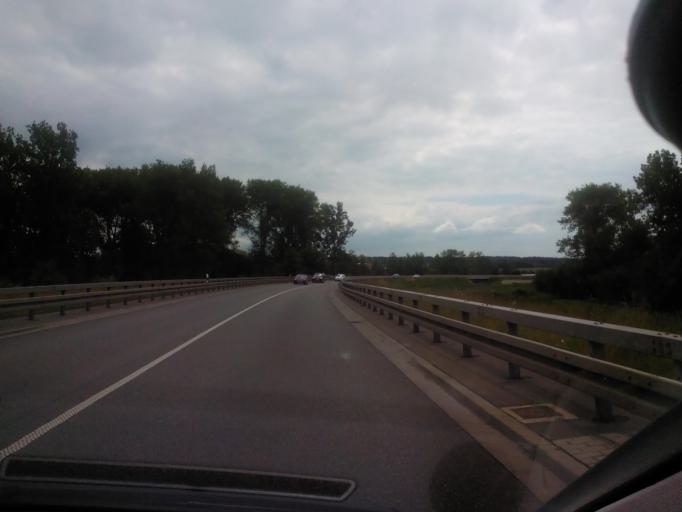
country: DE
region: Saarland
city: Uberherrn
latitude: 49.2582
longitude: 6.7324
